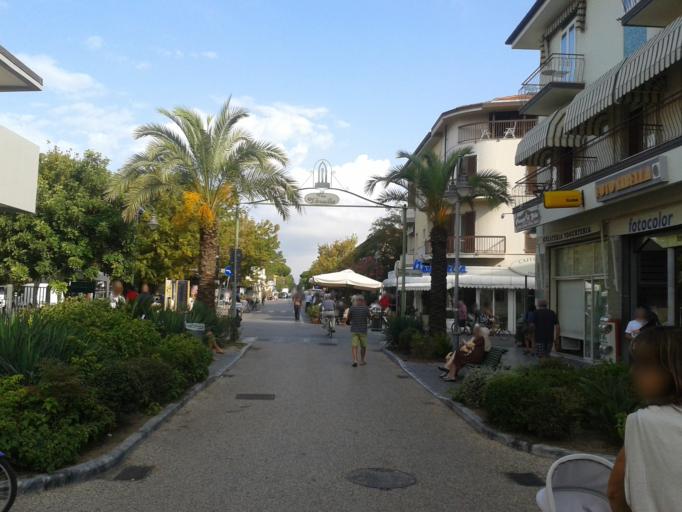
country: IT
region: Tuscany
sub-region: Provincia di Lucca
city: Pietrasanta
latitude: 43.9267
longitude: 10.2008
